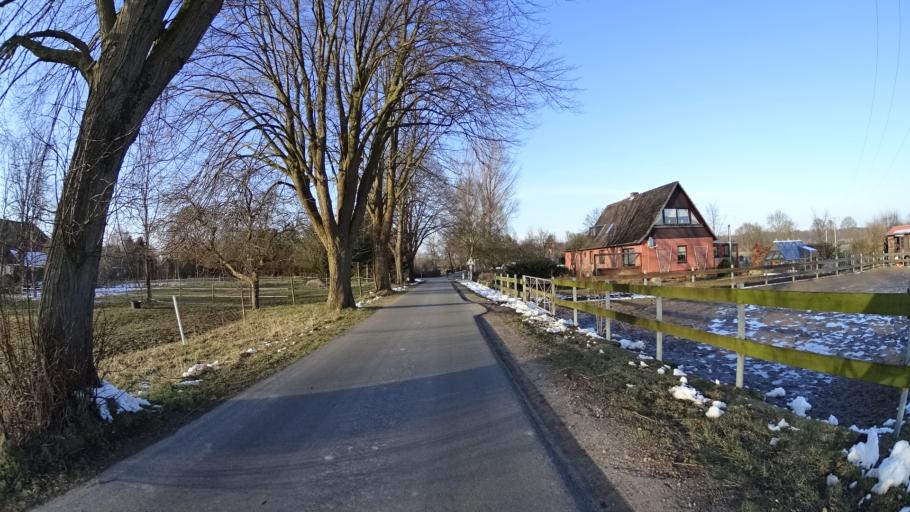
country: DE
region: Schleswig-Holstein
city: Fargau-Pratjau
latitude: 54.3420
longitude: 10.4080
